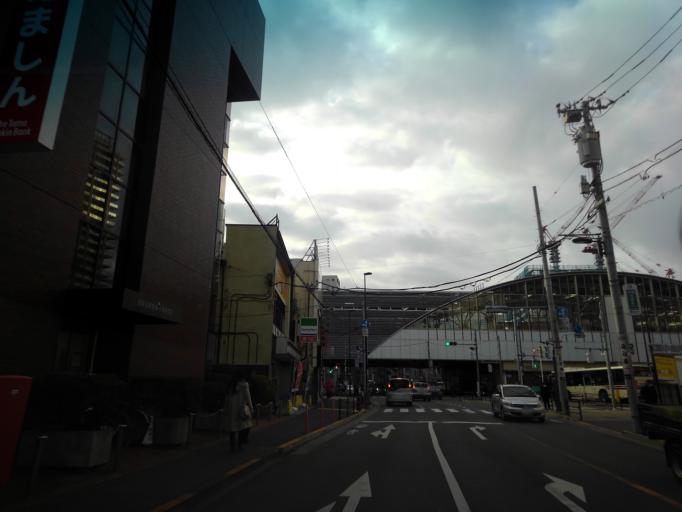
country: JP
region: Tokyo
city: Kokubunji
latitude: 35.7018
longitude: 139.5072
